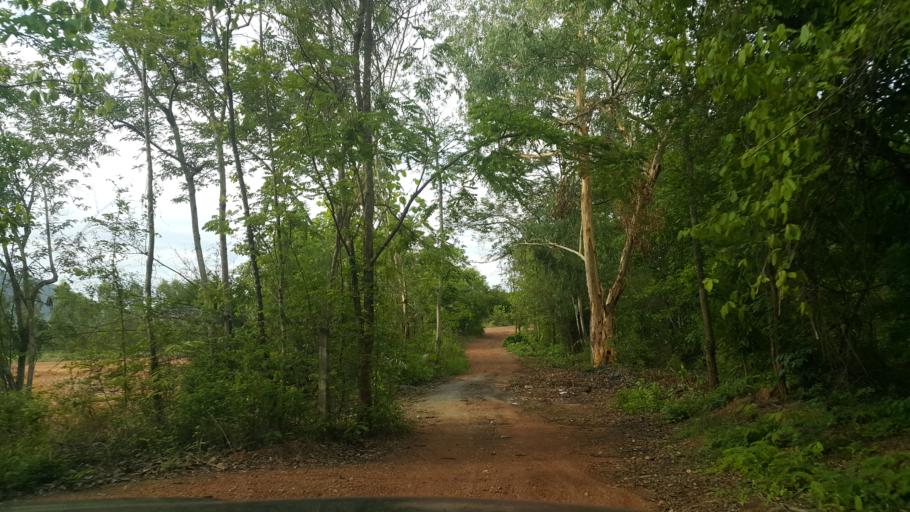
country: TH
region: Chiang Mai
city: Mae On
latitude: 18.7218
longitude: 99.2184
